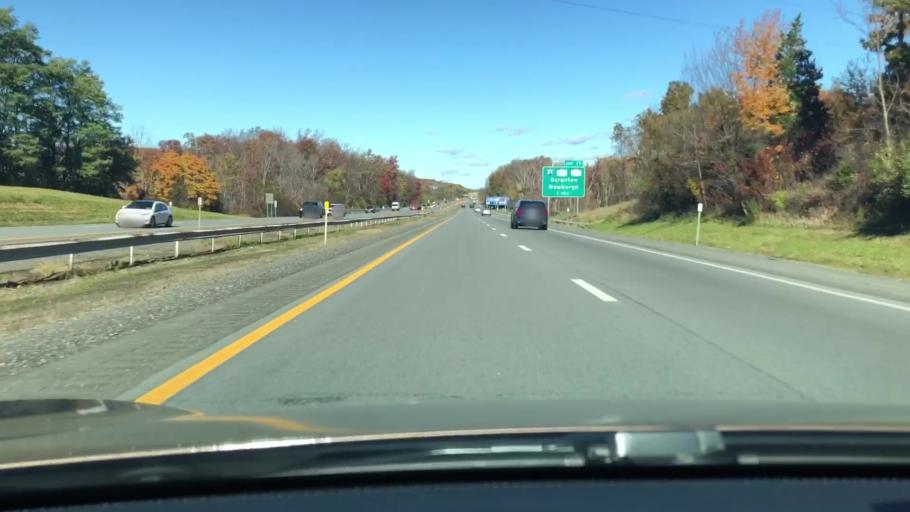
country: US
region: New York
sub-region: Orange County
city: Gardnertown
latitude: 41.4936
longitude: -74.0782
